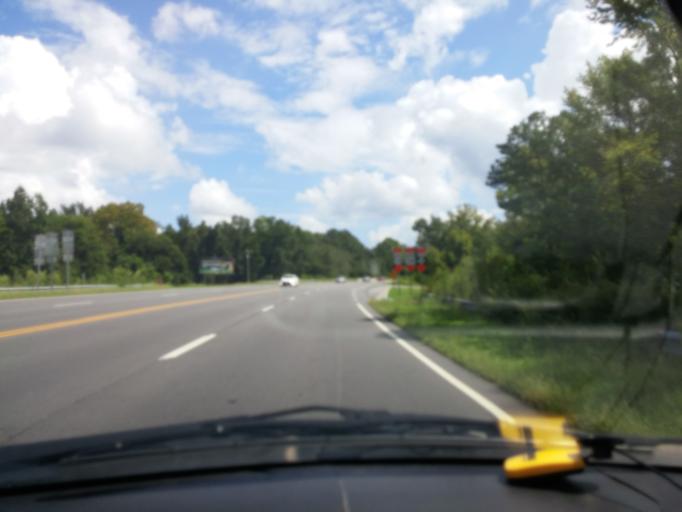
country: US
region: North Carolina
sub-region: Lenoir County
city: Kinston
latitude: 35.2584
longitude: -77.5932
